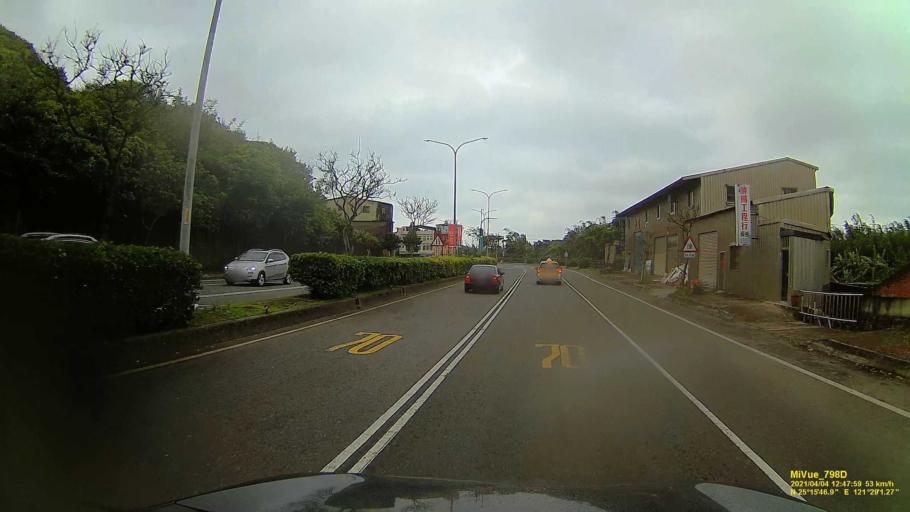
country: TW
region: Taipei
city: Taipei
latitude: 25.2632
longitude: 121.4834
